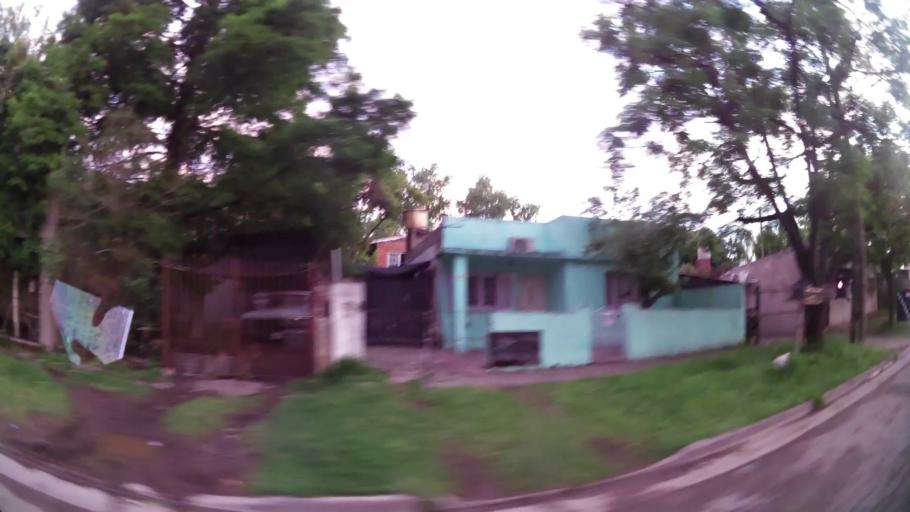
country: AR
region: Buenos Aires
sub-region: Partido de Lomas de Zamora
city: Lomas de Zamora
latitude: -34.7551
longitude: -58.3629
